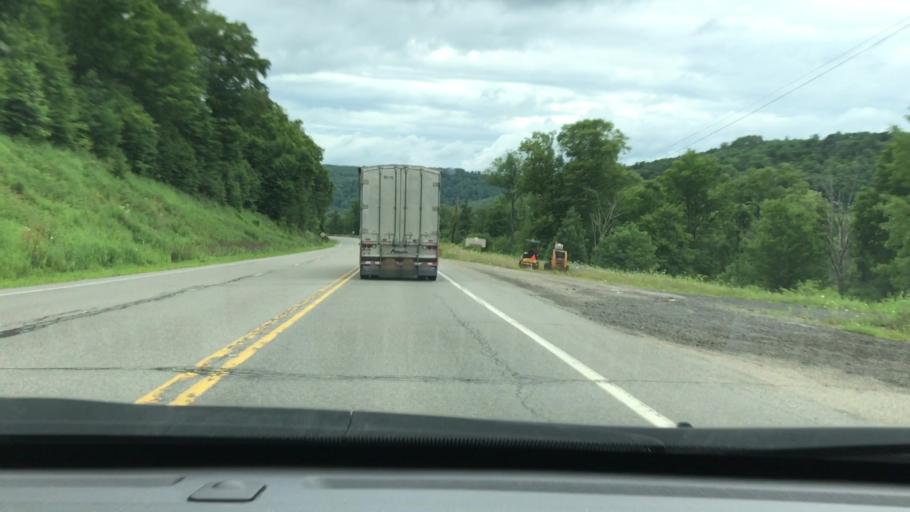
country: US
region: Pennsylvania
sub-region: McKean County
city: Kane
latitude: 41.7609
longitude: -78.7027
